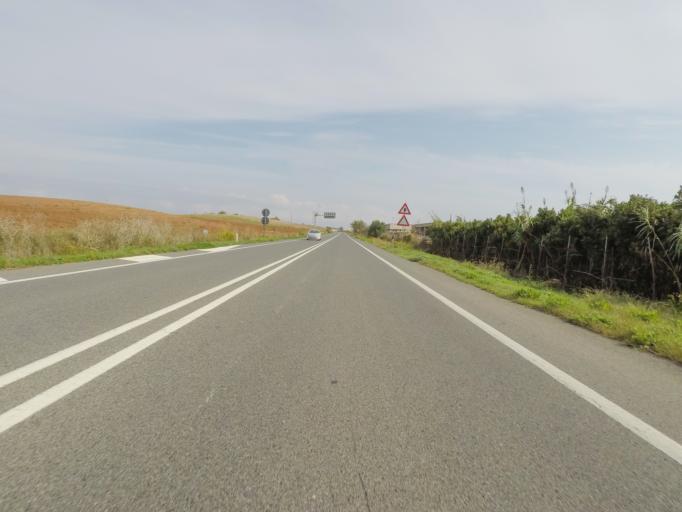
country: IT
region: Tuscany
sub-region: Provincia di Grosseto
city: Orbetello Scalo
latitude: 42.4145
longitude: 11.3319
